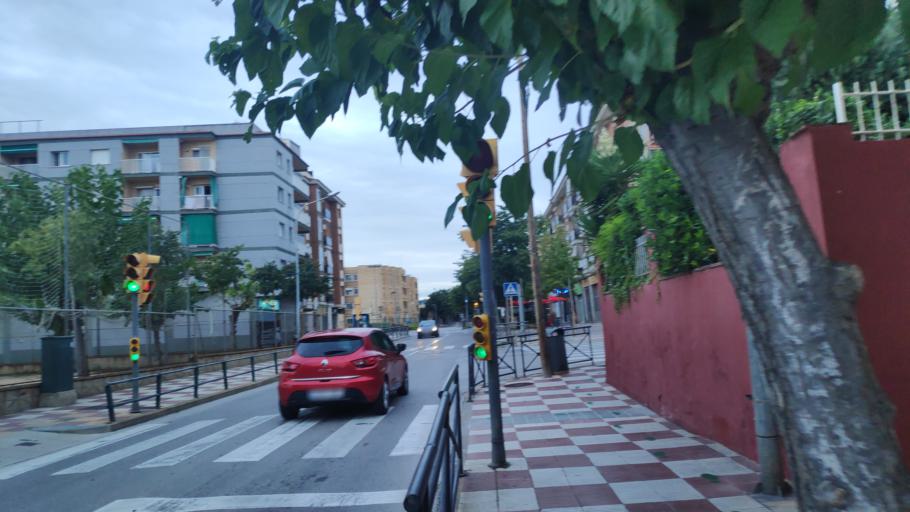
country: ES
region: Catalonia
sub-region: Provincia de Girona
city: Lloret de Mar
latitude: 41.7042
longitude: 2.8434
